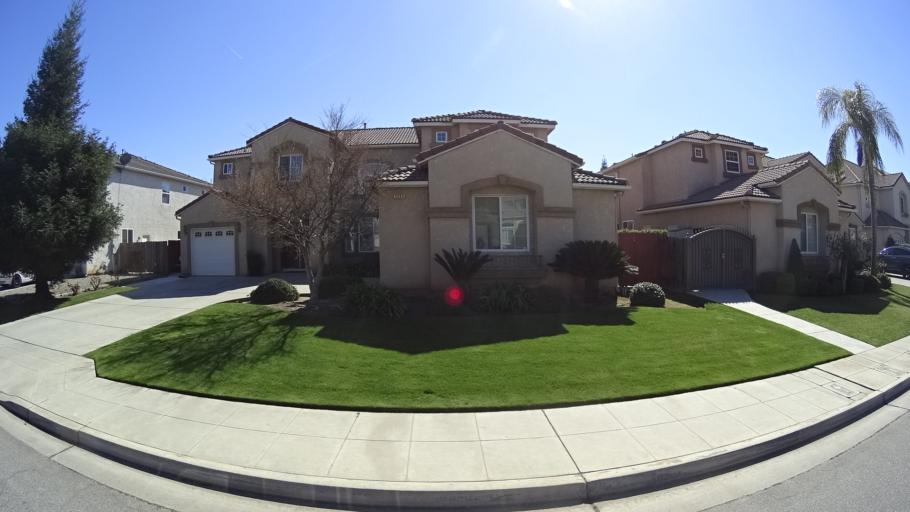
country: US
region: California
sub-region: Fresno County
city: Clovis
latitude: 36.8560
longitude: -119.7319
